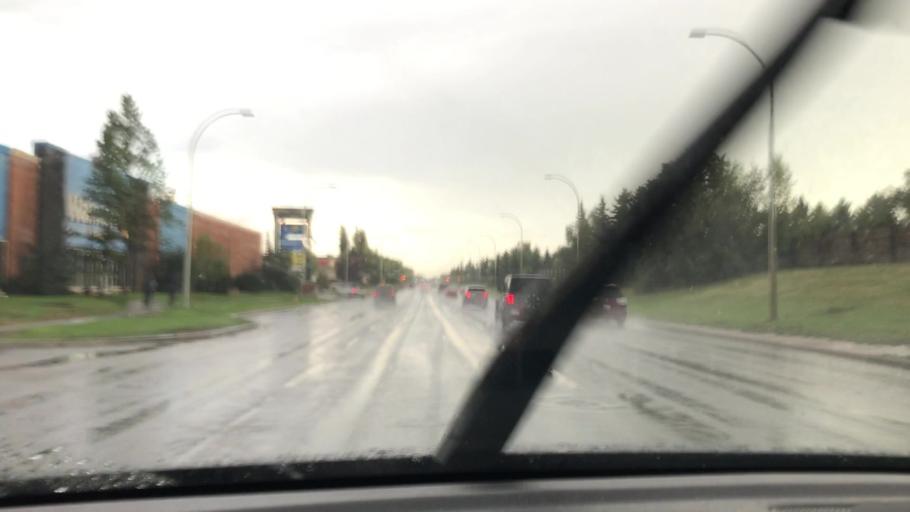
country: CA
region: Alberta
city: Edmonton
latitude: 53.4760
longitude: -113.4956
